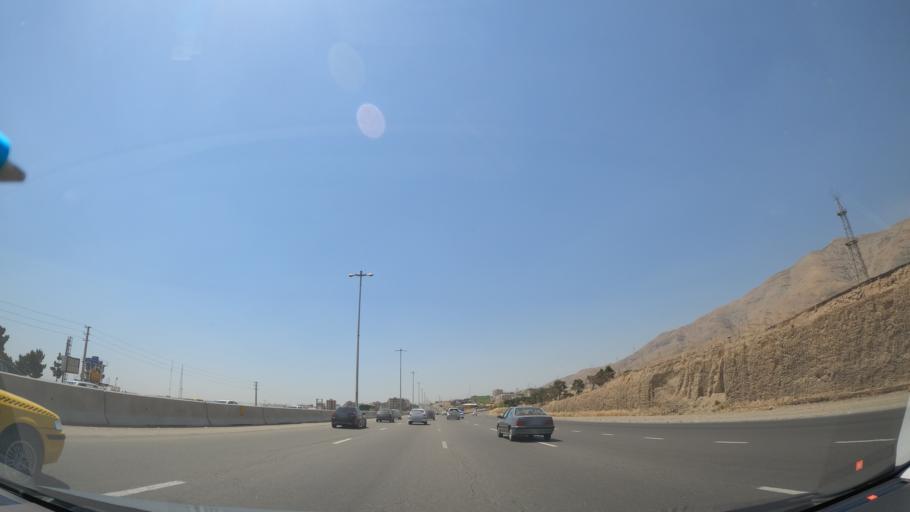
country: IR
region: Tehran
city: Shahr-e Qods
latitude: 35.7510
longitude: 51.0799
